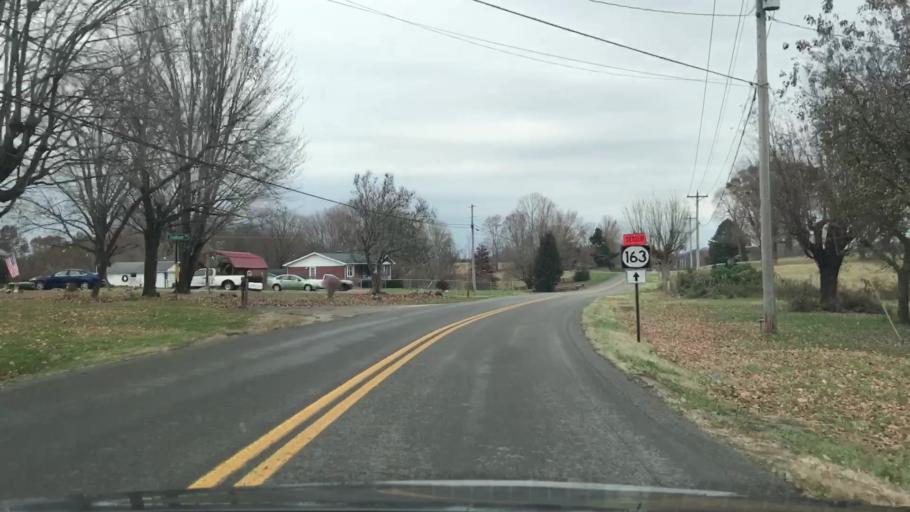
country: US
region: Kentucky
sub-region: Metcalfe County
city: Edmonton
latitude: 36.9511
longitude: -85.6149
